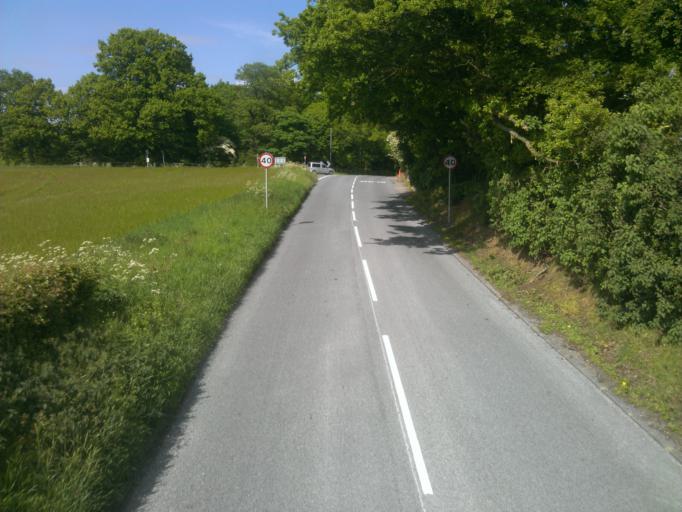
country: GB
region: England
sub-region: Suffolk
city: East Bergholt
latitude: 51.9591
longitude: 0.9642
